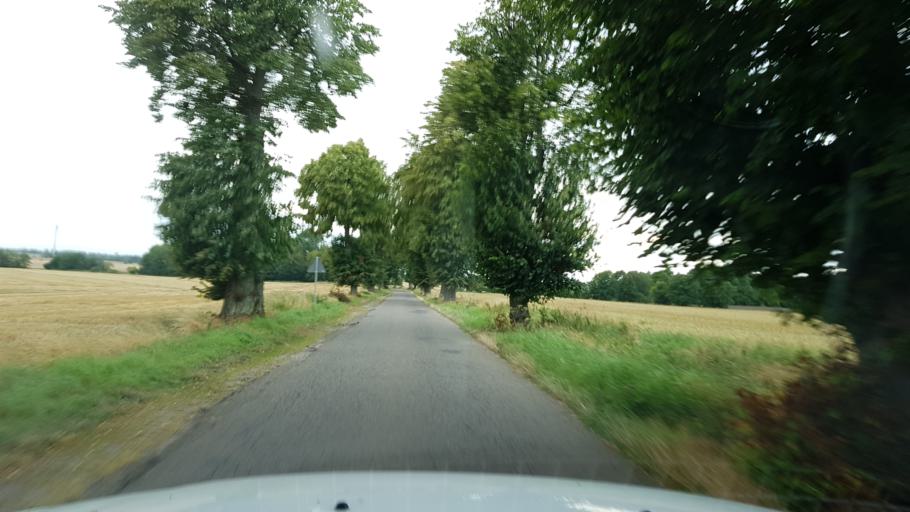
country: PL
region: West Pomeranian Voivodeship
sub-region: Powiat bialogardzki
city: Karlino
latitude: 54.1157
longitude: 15.8703
